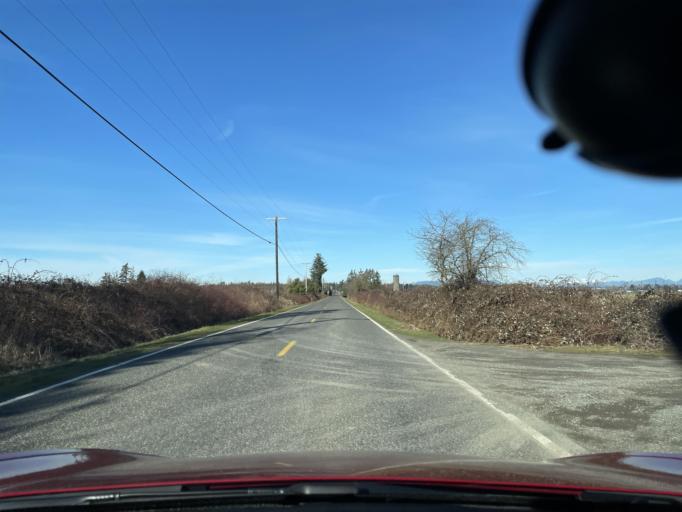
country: US
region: Washington
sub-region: Whatcom County
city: Lynden
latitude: 48.9611
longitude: -122.5303
